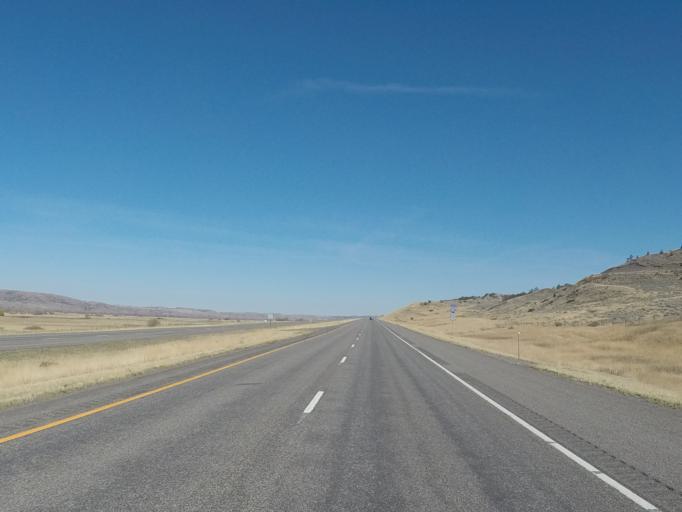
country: US
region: Montana
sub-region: Sweet Grass County
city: Big Timber
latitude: 45.7821
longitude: -110.0585
